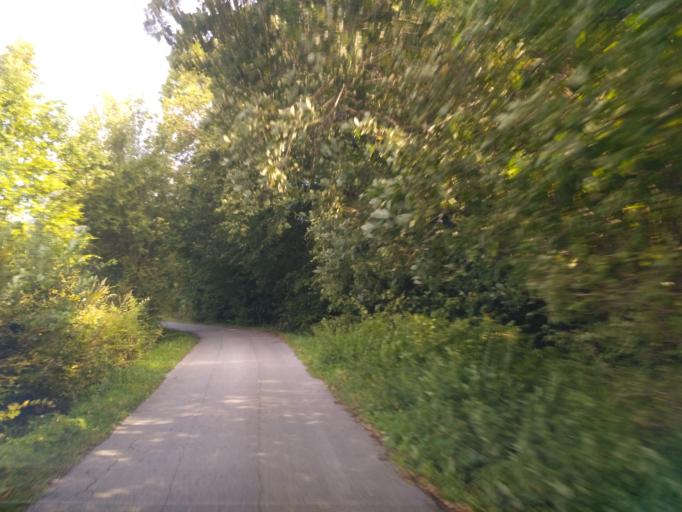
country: PL
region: Subcarpathian Voivodeship
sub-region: Powiat strzyzowski
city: Strzyzow
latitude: 49.8483
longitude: 21.8246
